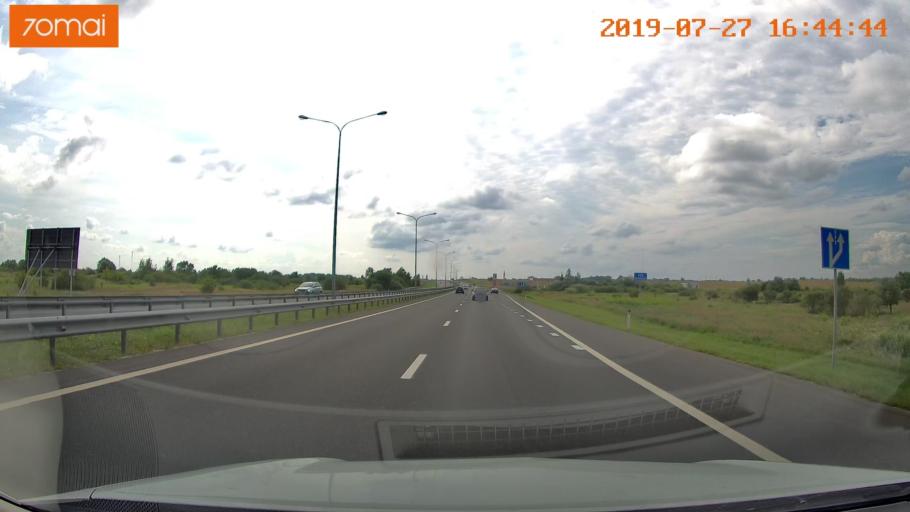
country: RU
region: Kaliningrad
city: Gvardeysk
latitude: 54.6720
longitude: 21.0663
